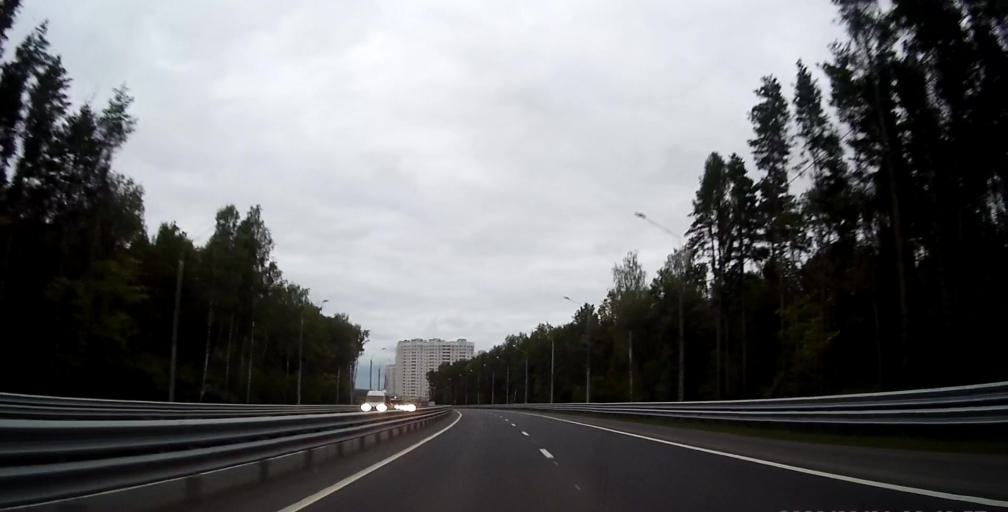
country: RU
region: Moskovskaya
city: Dubrovitsy
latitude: 55.4068
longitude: 37.5018
